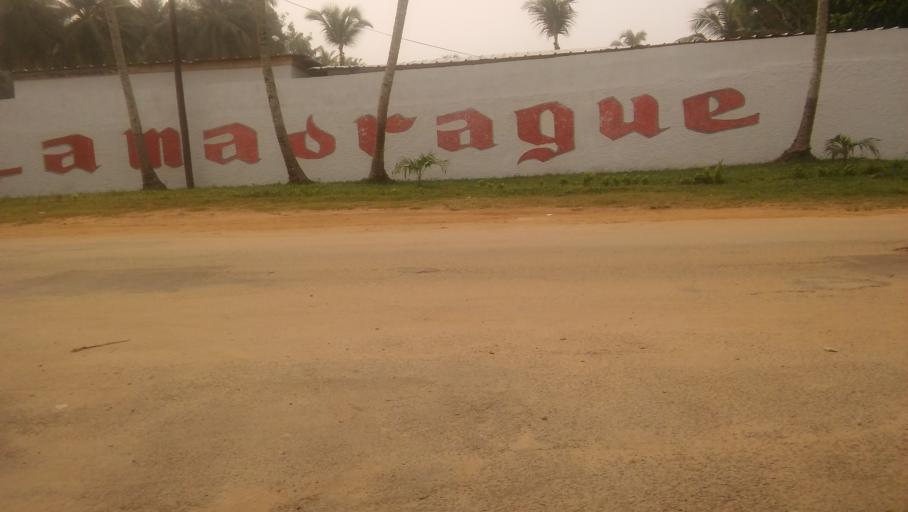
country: CI
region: Sud-Comoe
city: Grand-Bassam
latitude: 5.1962
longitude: -3.7408
